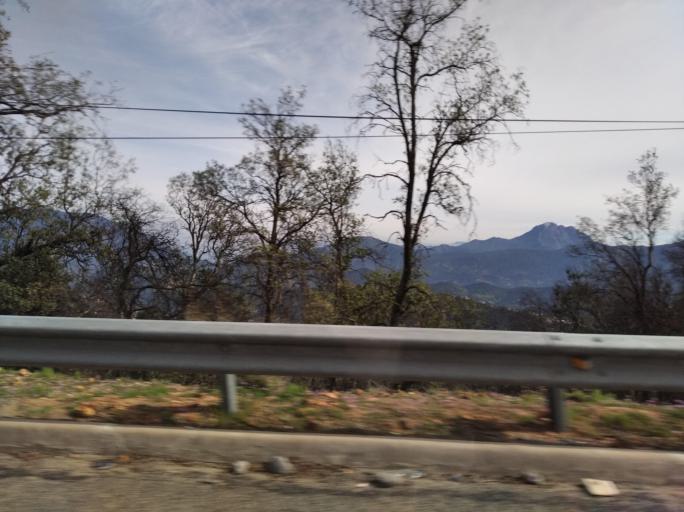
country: CL
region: Valparaiso
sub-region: Provincia de San Felipe
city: Llaillay
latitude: -33.0629
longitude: -71.0116
